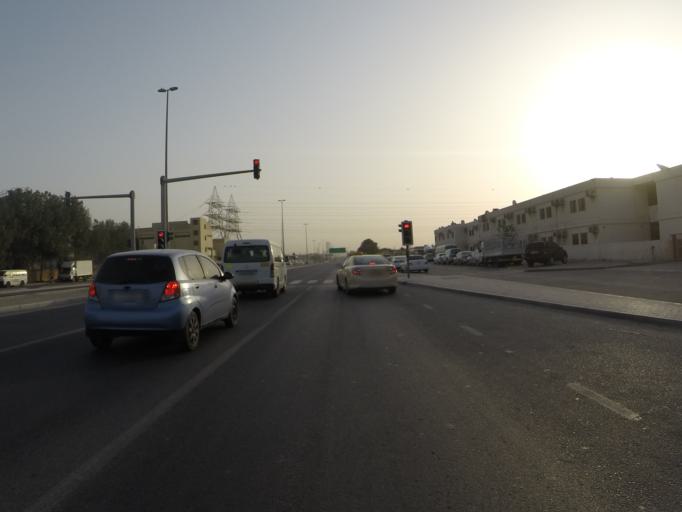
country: AE
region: Dubai
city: Dubai
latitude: 25.1353
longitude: 55.2370
